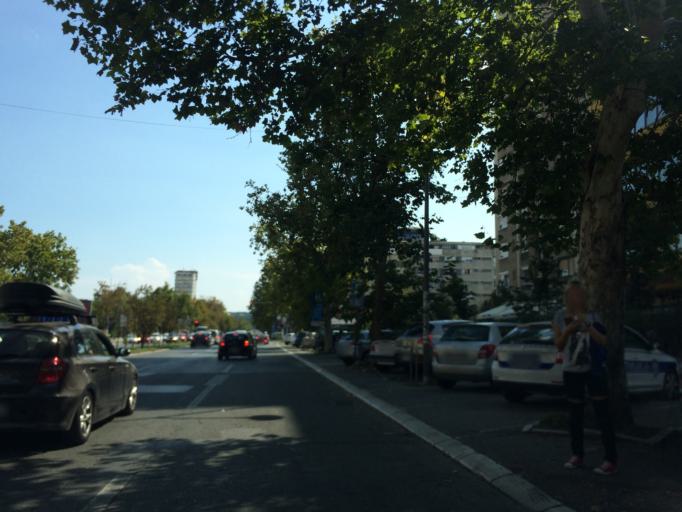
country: RS
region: Autonomna Pokrajina Vojvodina
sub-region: Juznobacki Okrug
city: Novi Sad
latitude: 45.2475
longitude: 19.8393
